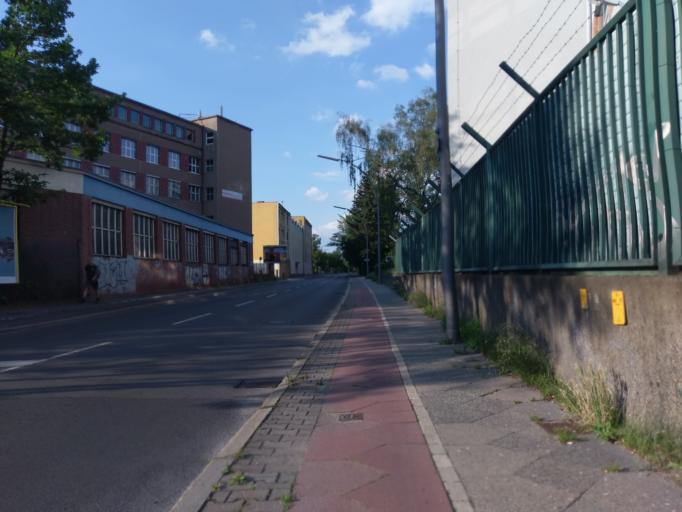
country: DE
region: Brandenburg
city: Teltow
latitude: 52.4110
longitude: 13.2752
